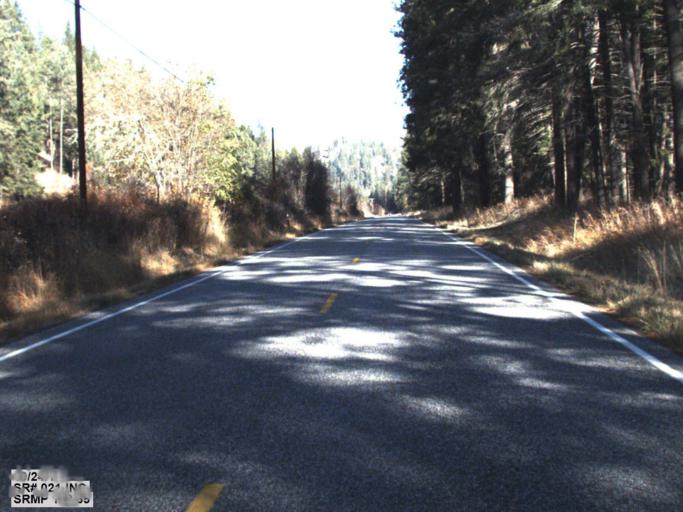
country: CA
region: British Columbia
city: Grand Forks
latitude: 48.9680
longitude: -118.5271
